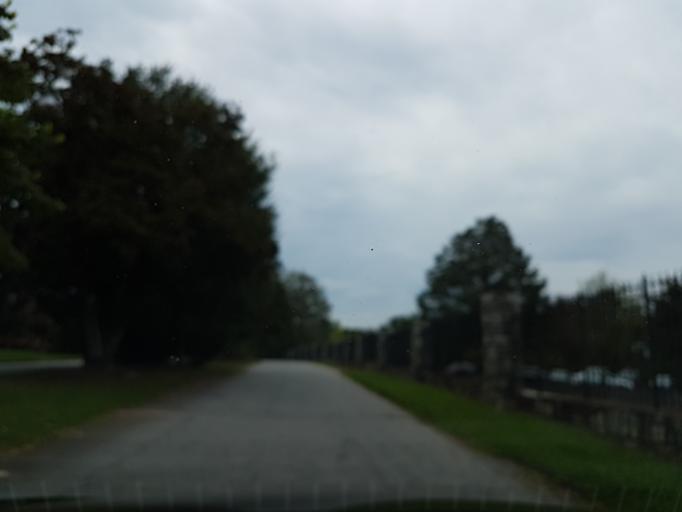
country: US
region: Georgia
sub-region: DeKalb County
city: North Atlanta
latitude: 33.8752
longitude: -84.3308
